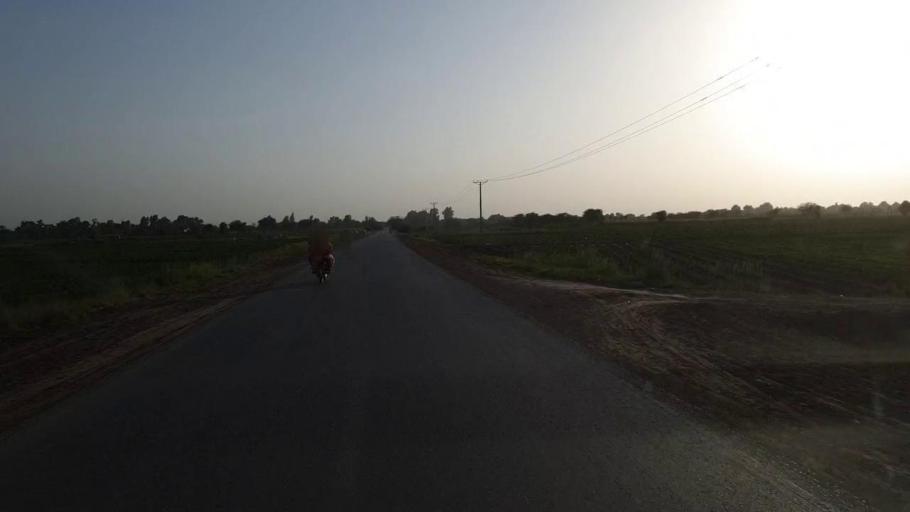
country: PK
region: Sindh
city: Jam Sahib
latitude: 26.2774
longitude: 68.5651
